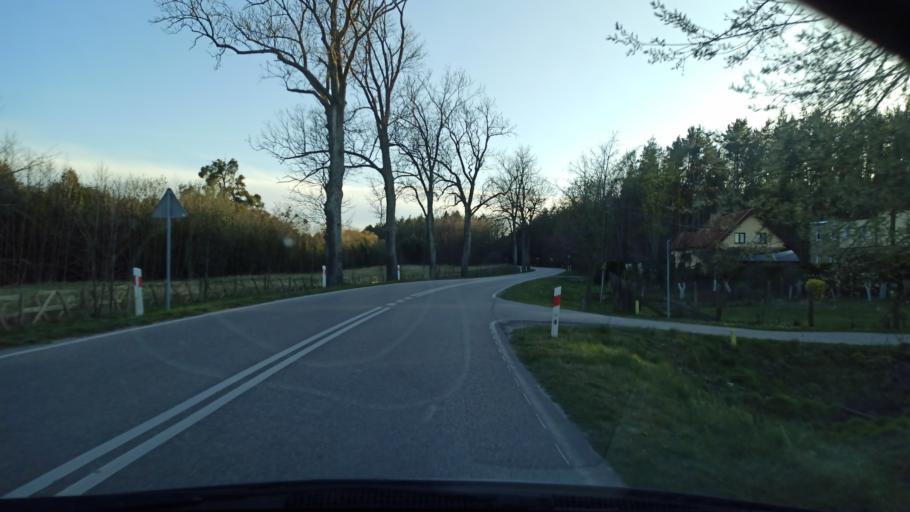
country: PL
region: Warmian-Masurian Voivodeship
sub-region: Powiat elblaski
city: Tolkmicko
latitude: 54.3036
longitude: 19.5072
